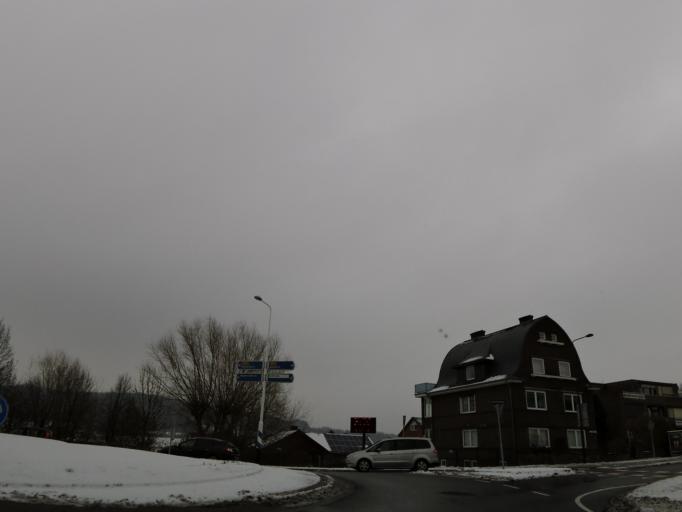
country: NL
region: Limburg
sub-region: Gemeente Vaals
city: Vaals
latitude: 50.7773
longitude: 6.0071
